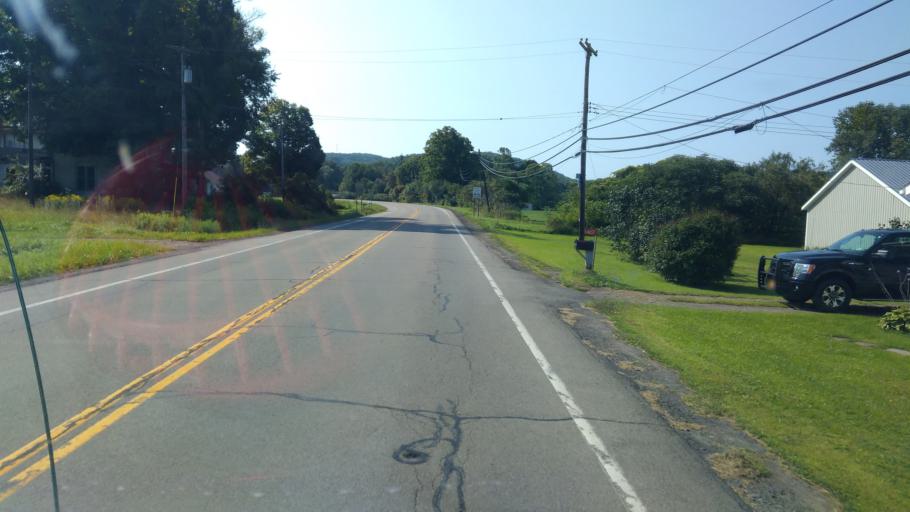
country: US
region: New York
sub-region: Allegany County
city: Cuba
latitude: 42.2035
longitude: -78.2749
